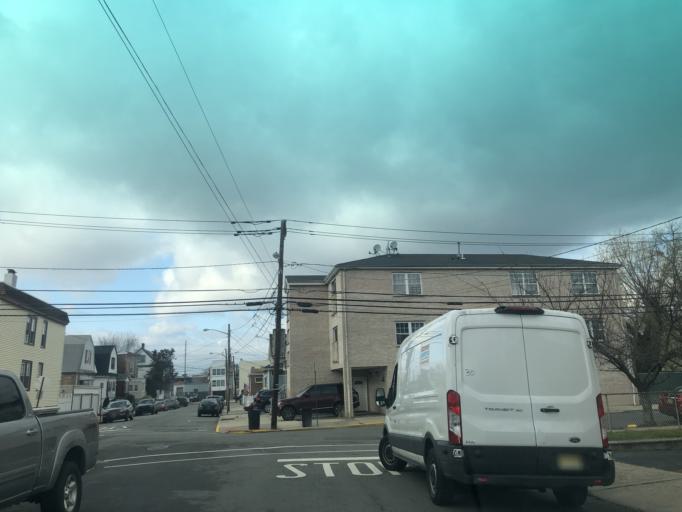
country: US
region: New Jersey
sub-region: Hudson County
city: Union City
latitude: 40.7826
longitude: -74.0311
